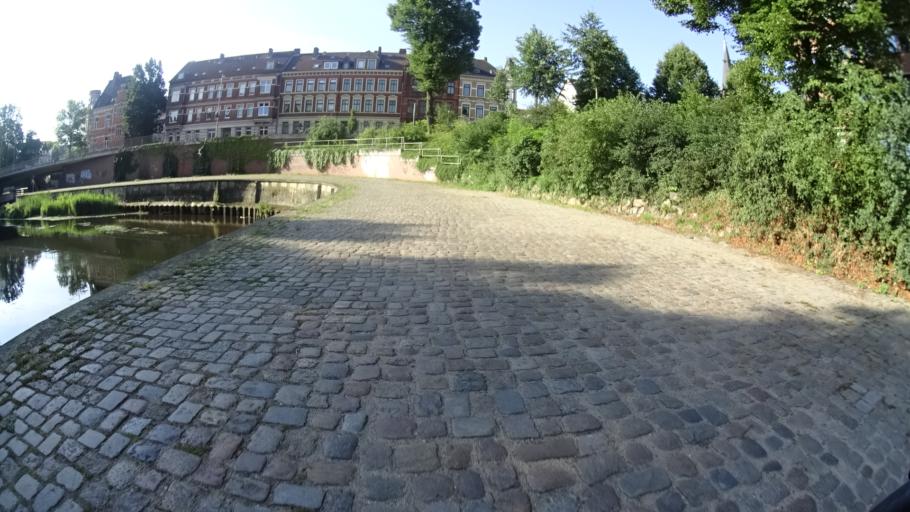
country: DE
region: Lower Saxony
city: Lueneburg
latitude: 53.2533
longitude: 10.4120
